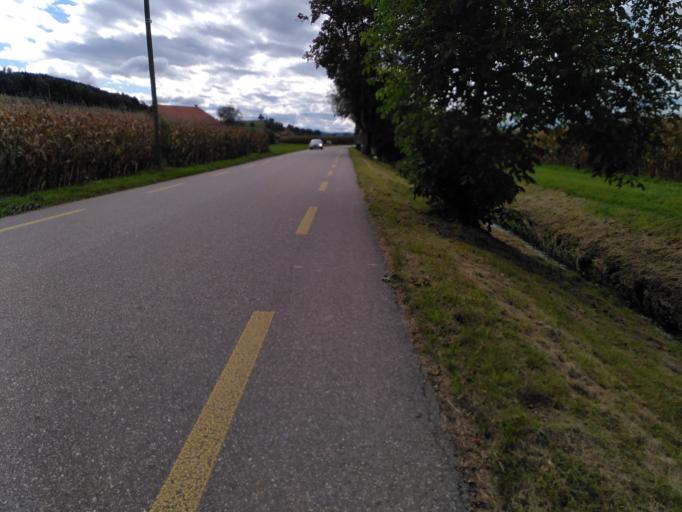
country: CH
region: Bern
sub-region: Emmental District
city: Ersigen
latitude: 47.1103
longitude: 7.6103
